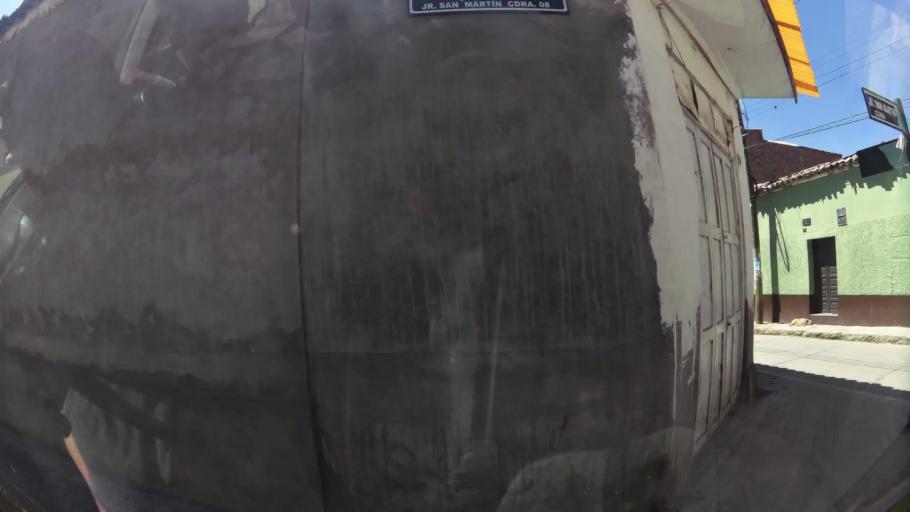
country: PE
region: Junin
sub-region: Provincia de Jauja
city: Jauja
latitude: -11.7745
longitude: -75.4981
